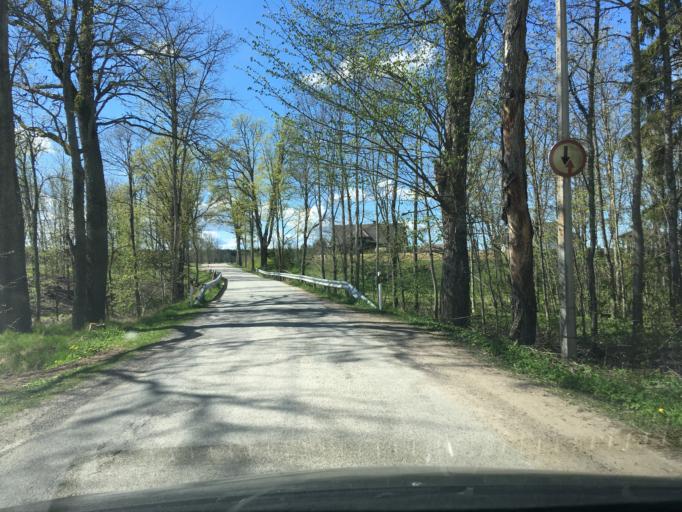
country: EE
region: Harju
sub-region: Rae vald
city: Vaida
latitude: 59.2036
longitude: 25.0955
